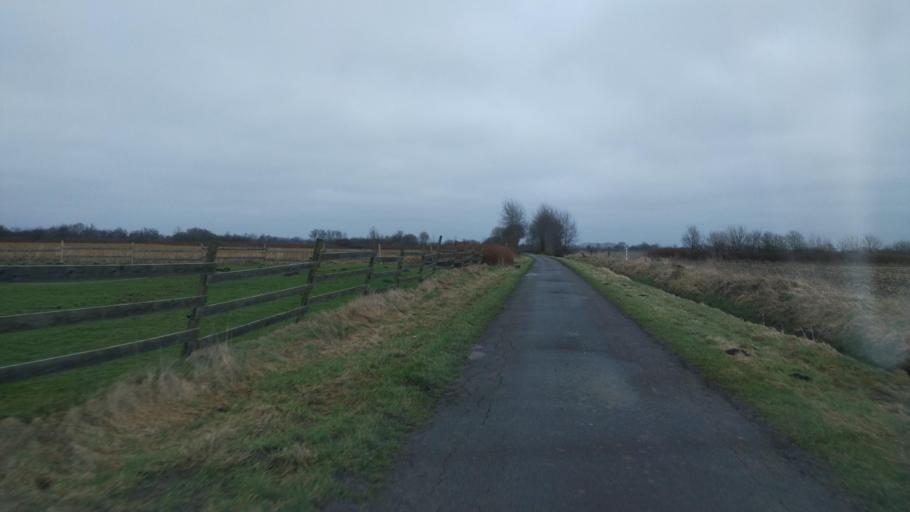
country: DE
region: Schleswig-Holstein
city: Hollingstedt
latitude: 54.4788
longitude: 9.3454
